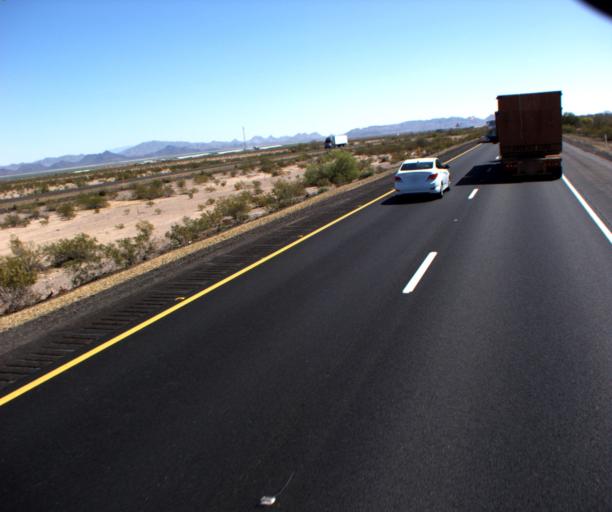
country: US
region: Arizona
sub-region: La Paz County
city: Salome
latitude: 33.6348
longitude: -113.7952
